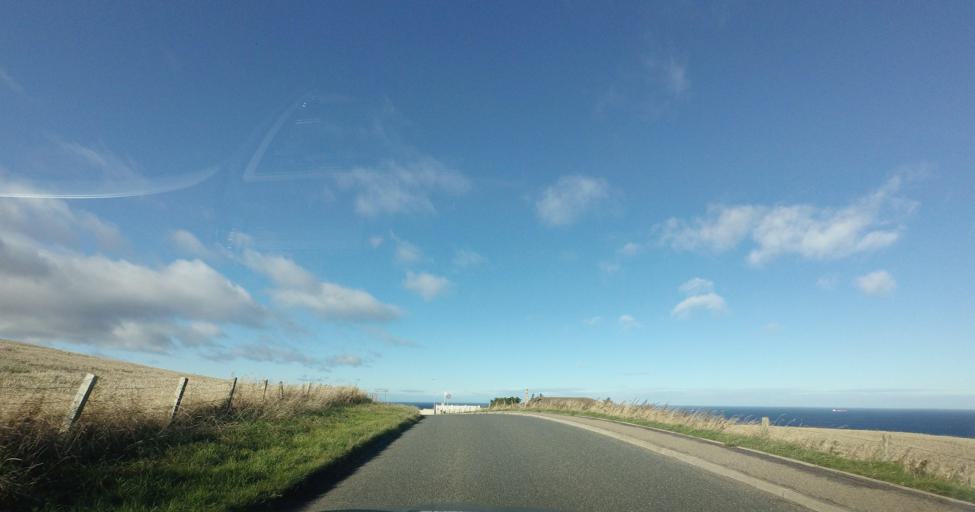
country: GB
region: Scotland
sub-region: Aberdeenshire
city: Macduff
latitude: 57.6707
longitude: -2.3291
